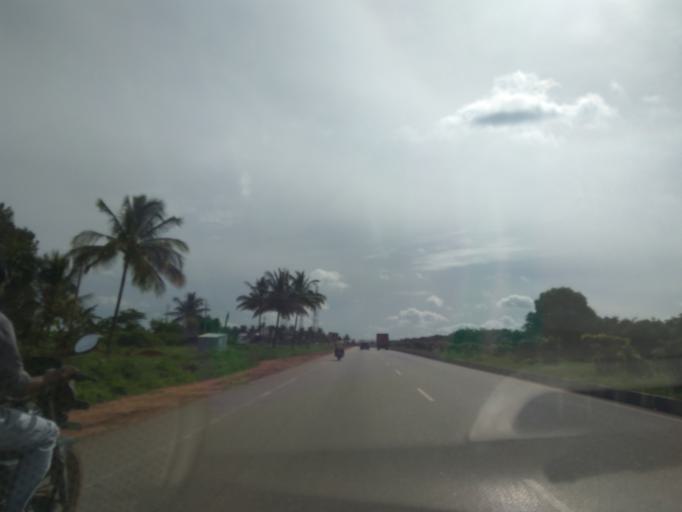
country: IN
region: Karnataka
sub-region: Bangalore Rural
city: Dasarahalli
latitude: 13.0888
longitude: 77.8324
